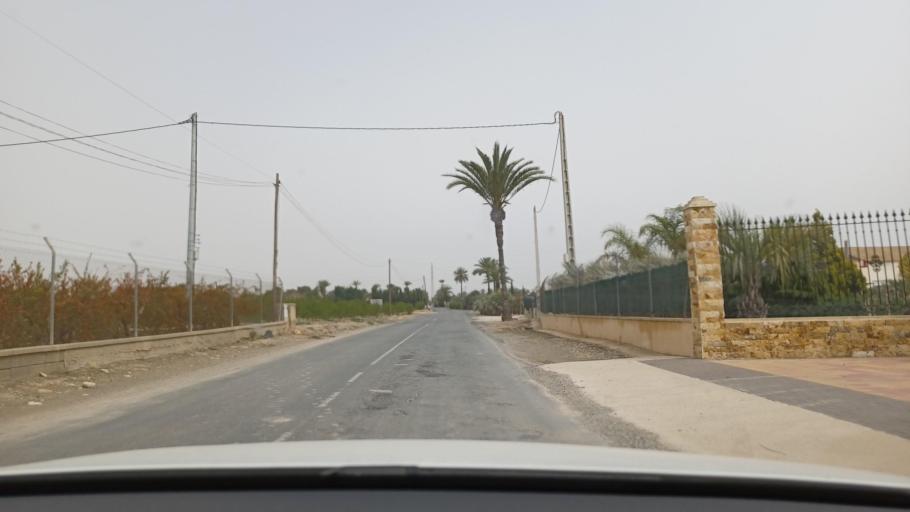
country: ES
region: Valencia
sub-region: Provincia de Alicante
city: Elche
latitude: 38.2261
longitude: -0.6947
